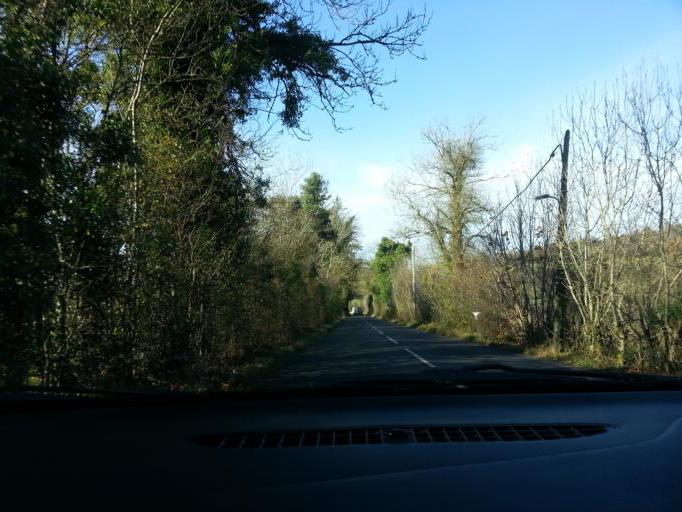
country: GB
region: Northern Ireland
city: Lisnaskea
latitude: 54.2245
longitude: -7.3517
